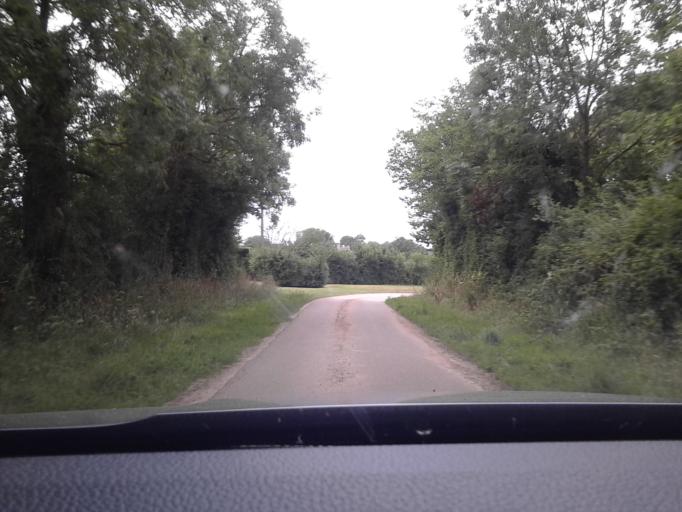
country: FR
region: Lower Normandy
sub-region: Departement de la Manche
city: Valognes
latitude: 49.5067
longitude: -1.4437
